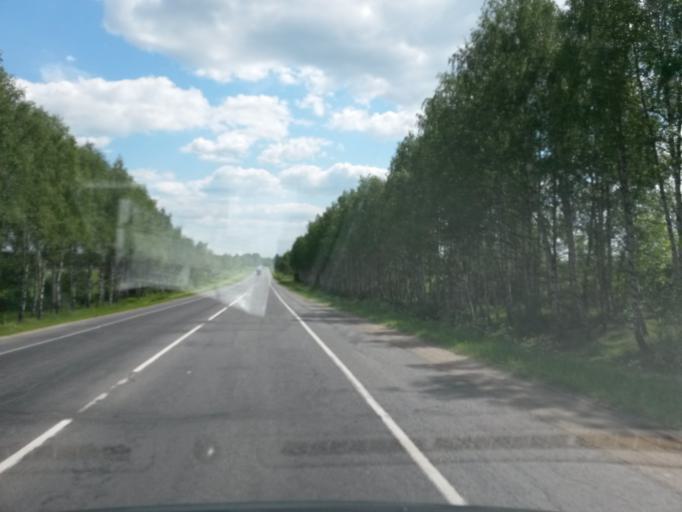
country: RU
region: Jaroslavl
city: Yaroslavl
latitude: 57.5577
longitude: 39.8624
